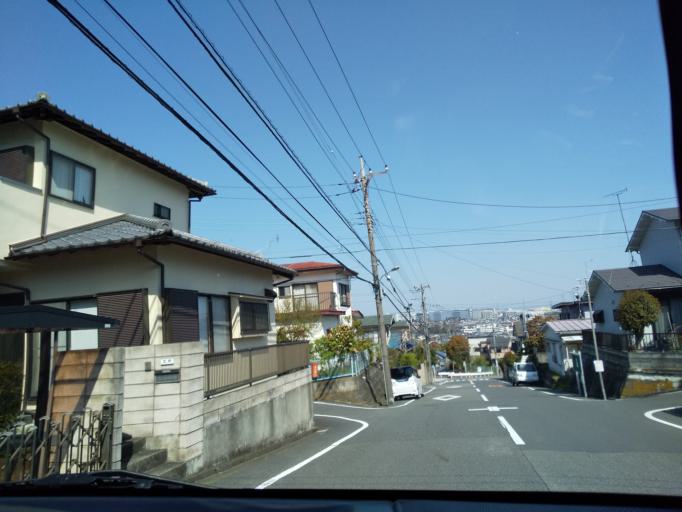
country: JP
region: Tokyo
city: Hino
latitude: 35.6415
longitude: 139.3763
